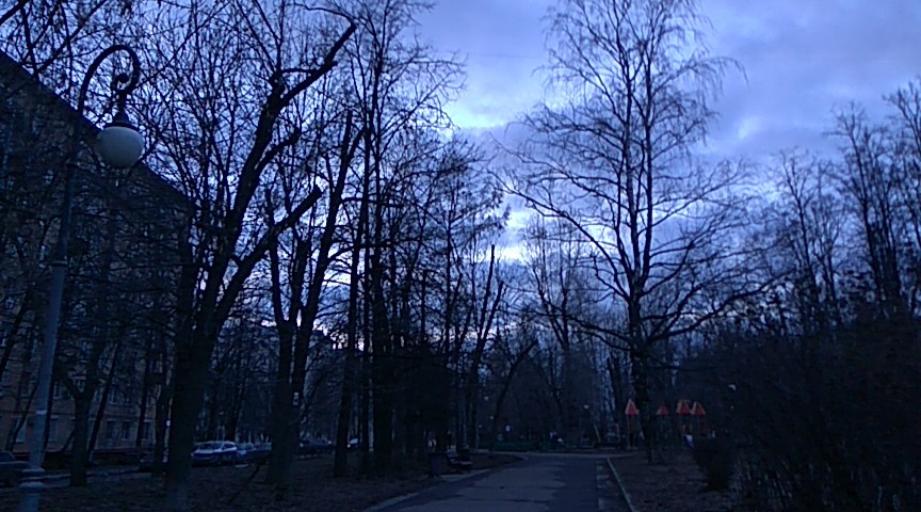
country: RU
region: Moskovskaya
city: Semenovskoye
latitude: 55.6935
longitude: 37.5468
